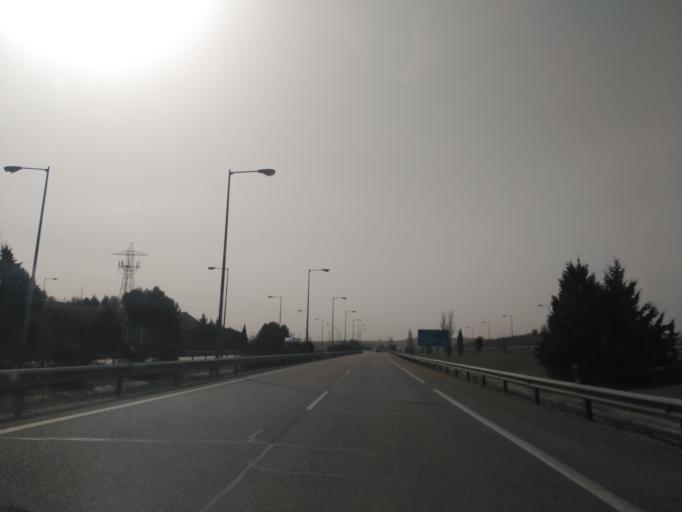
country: ES
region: Castille and Leon
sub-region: Provincia de Valladolid
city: Zaratan
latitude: 41.6580
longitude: -4.7625
